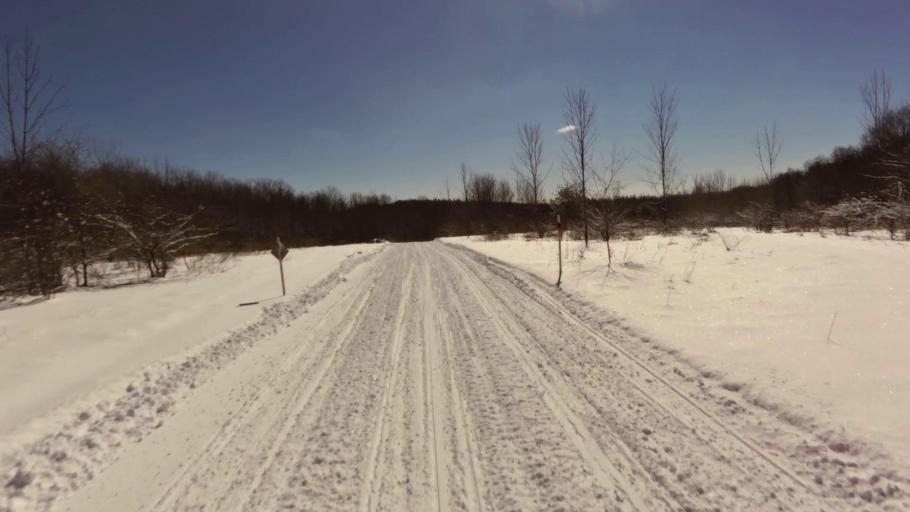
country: US
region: New York
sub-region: Chautauqua County
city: Mayville
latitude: 42.2327
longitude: -79.3934
